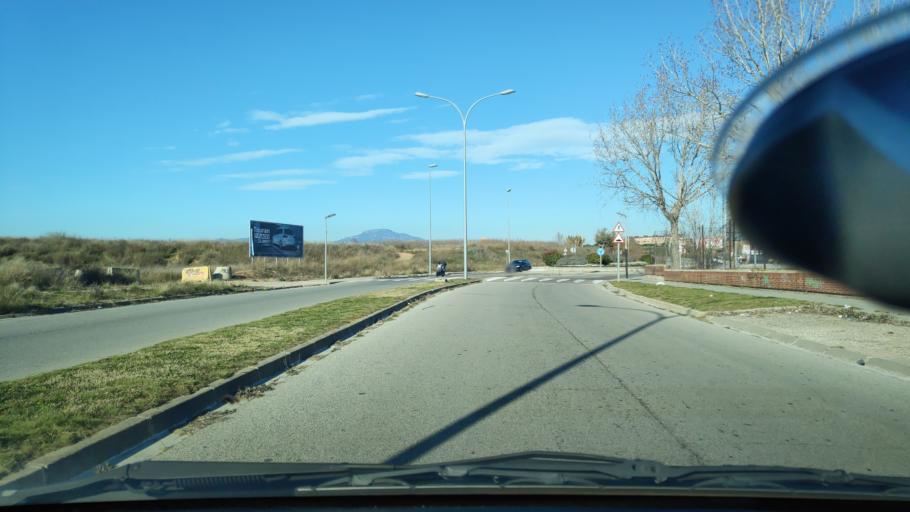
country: ES
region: Catalonia
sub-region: Provincia de Barcelona
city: Barbera del Valles
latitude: 41.5157
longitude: 2.1123
